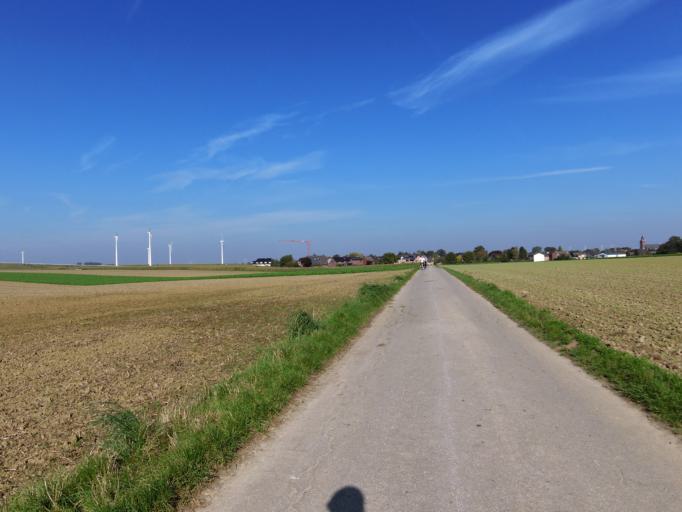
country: DE
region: North Rhine-Westphalia
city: Baesweiler
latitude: 50.9177
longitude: 6.1582
